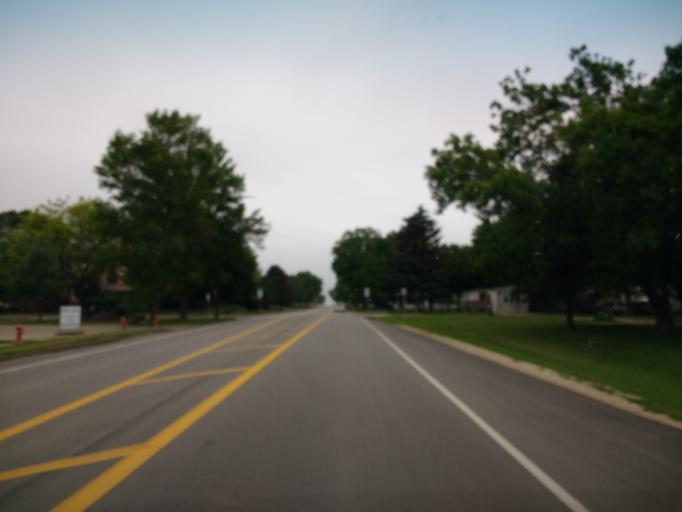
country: US
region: Iowa
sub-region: O'Brien County
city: Sanborn
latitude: 43.1861
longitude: -95.6510
